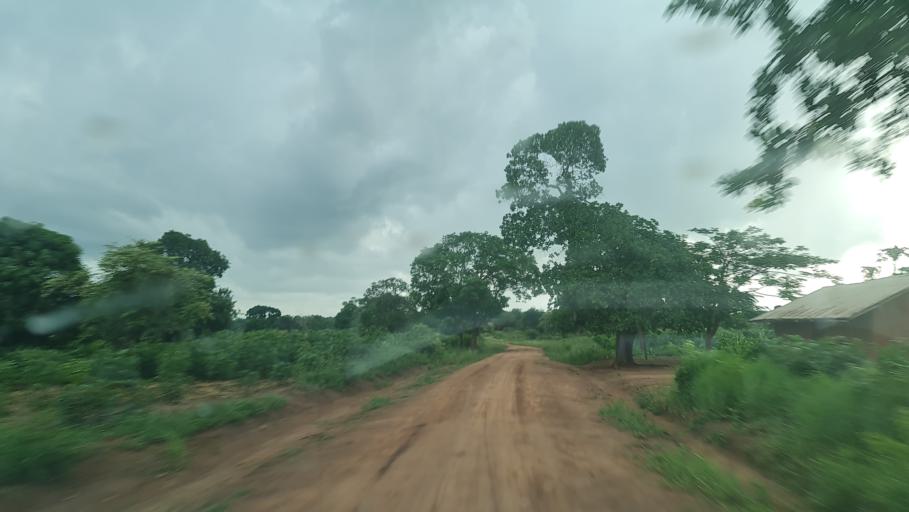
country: MZ
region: Nampula
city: Nacala
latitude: -13.9972
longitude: 40.3629
